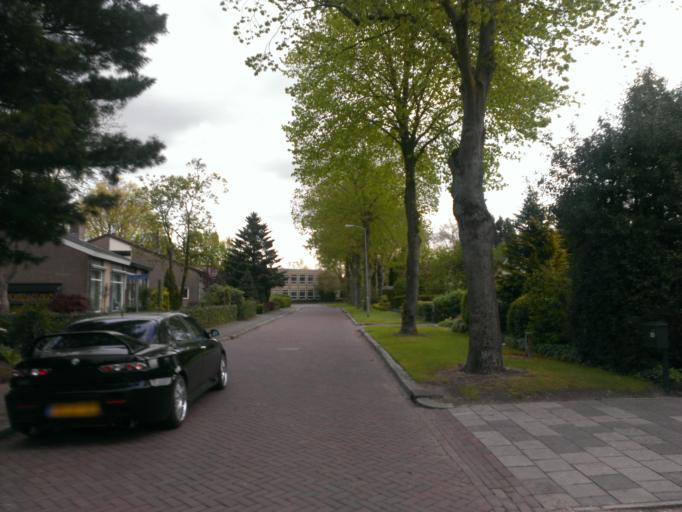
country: NL
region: Gelderland
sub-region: Gemeente Heerde
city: Heerde
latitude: 52.3937
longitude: 6.0443
